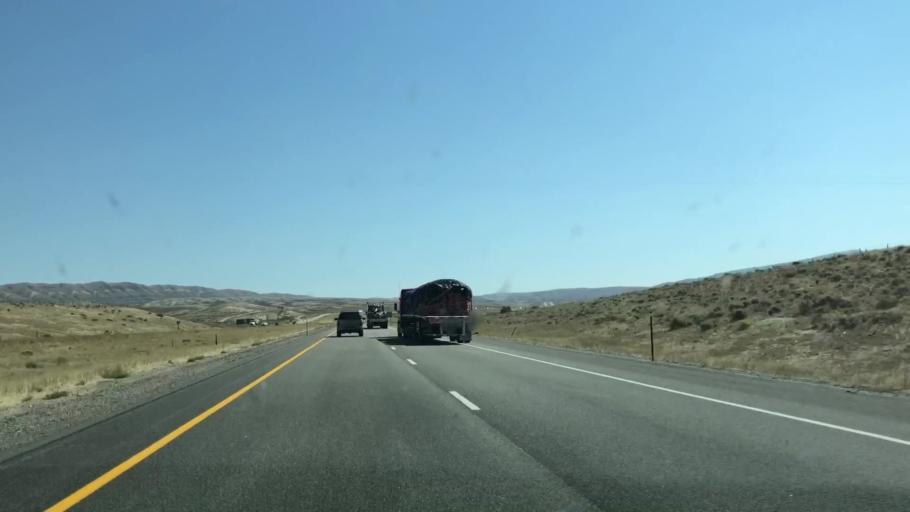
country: US
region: Wyoming
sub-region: Carbon County
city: Saratoga
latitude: 41.7413
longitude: -106.7892
